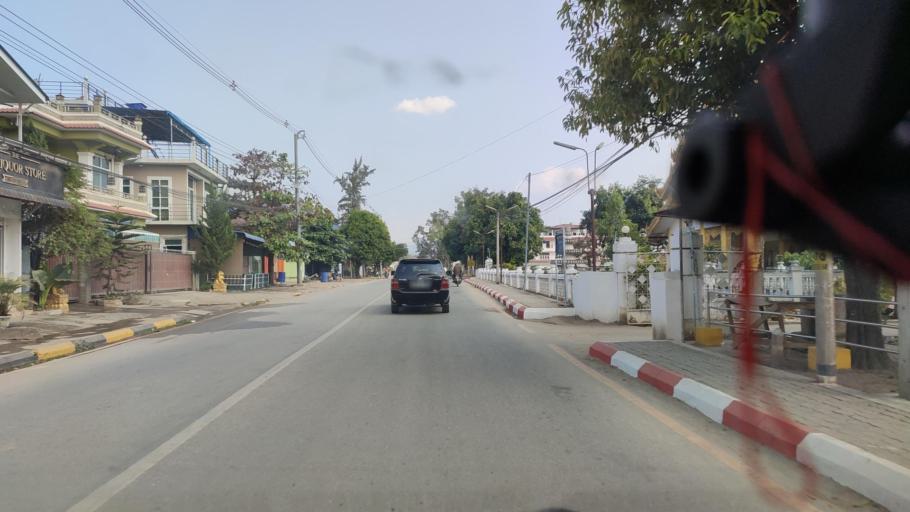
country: TH
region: Chiang Rai
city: Mae Sai
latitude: 21.2971
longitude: 99.6118
